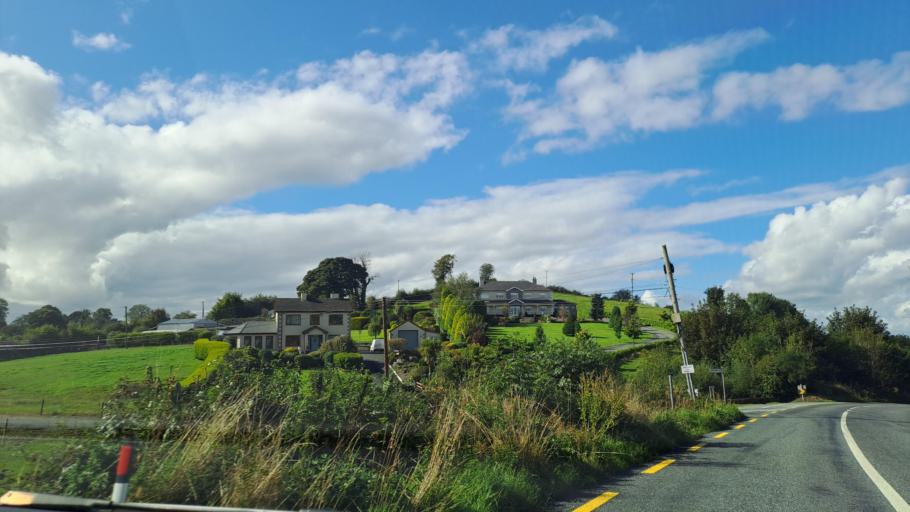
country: IE
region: Ulster
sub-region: An Cabhan
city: Kingscourt
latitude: 53.9681
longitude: -6.8649
